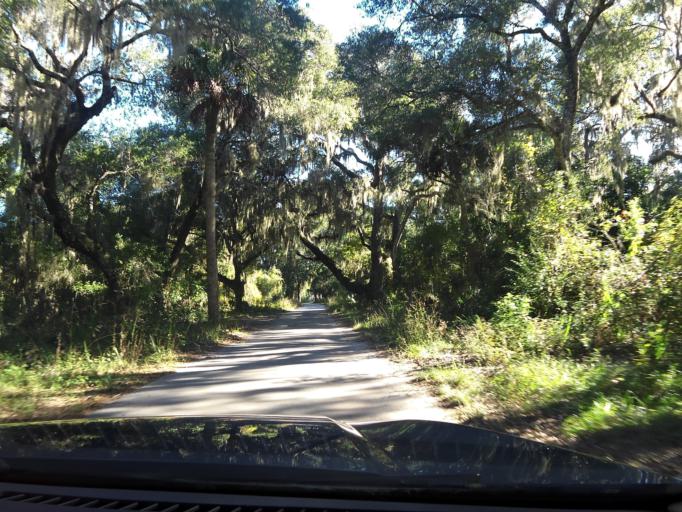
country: US
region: Florida
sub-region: Duval County
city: Atlantic Beach
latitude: 30.4300
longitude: -81.4266
